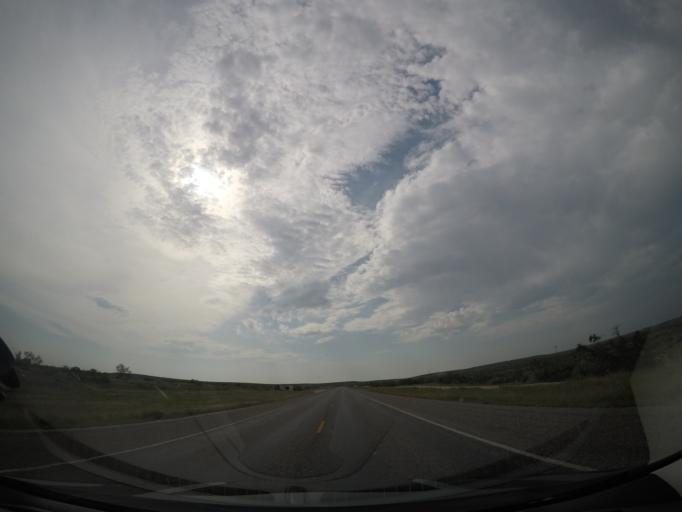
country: US
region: Texas
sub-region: Val Verde County
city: Cienegas Terrace
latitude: 29.7811
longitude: -101.3993
